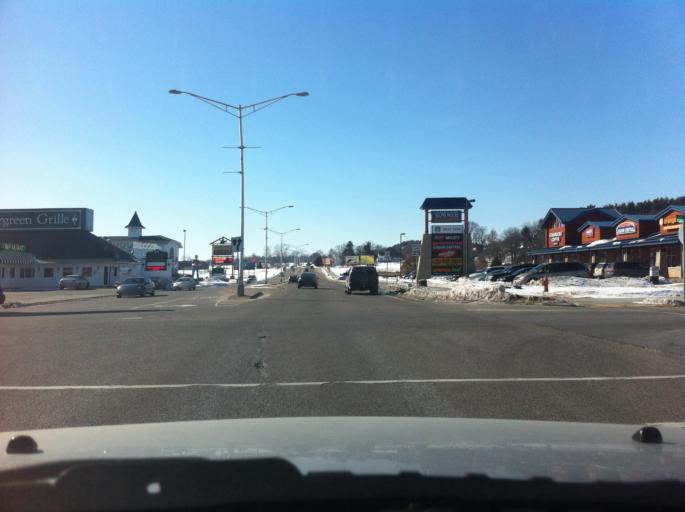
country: US
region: Wisconsin
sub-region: Sauk County
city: Lake Delton
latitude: 43.5758
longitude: -89.7802
